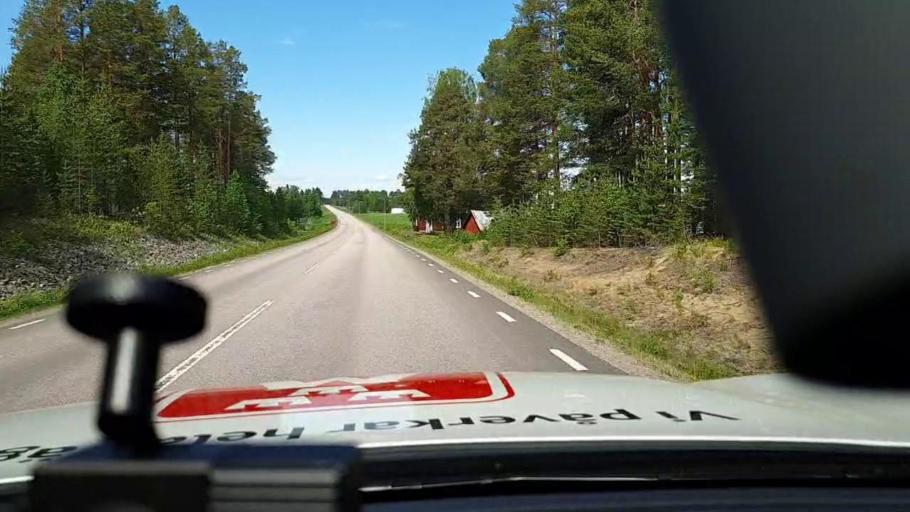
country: SE
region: Norrbotten
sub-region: Lulea Kommun
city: Sodra Sunderbyn
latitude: 65.6364
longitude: 21.9150
